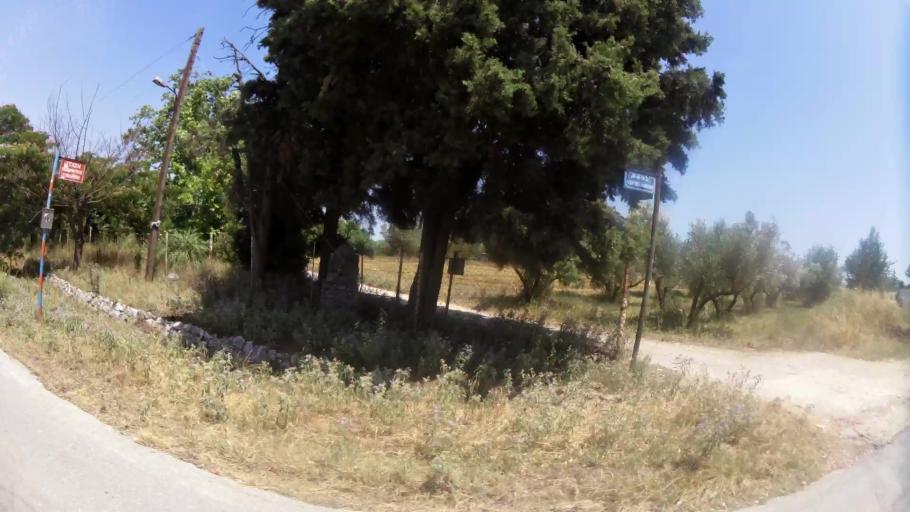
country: GR
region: Central Macedonia
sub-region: Nomos Thessalonikis
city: Nea Michaniona
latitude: 40.4732
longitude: 22.8748
